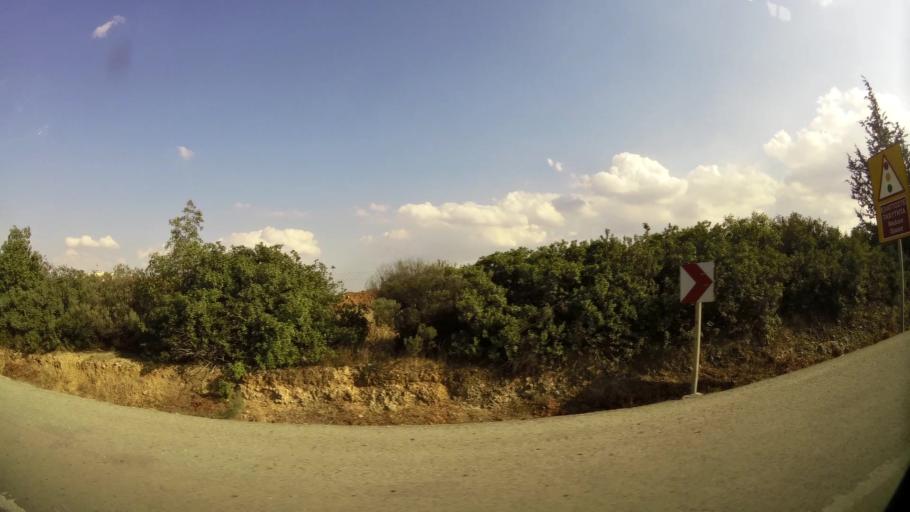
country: CY
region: Lefkosia
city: Kato Deftera
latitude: 35.1263
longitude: 33.2969
